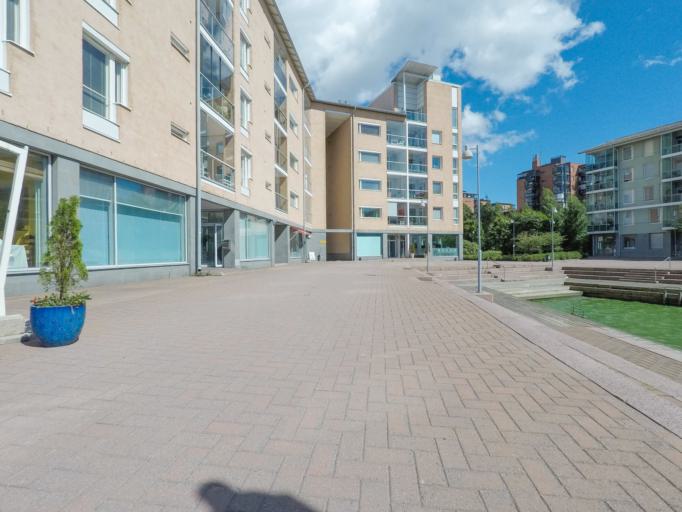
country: FI
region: Uusimaa
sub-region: Helsinki
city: Helsinki
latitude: 60.1879
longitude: 25.0304
